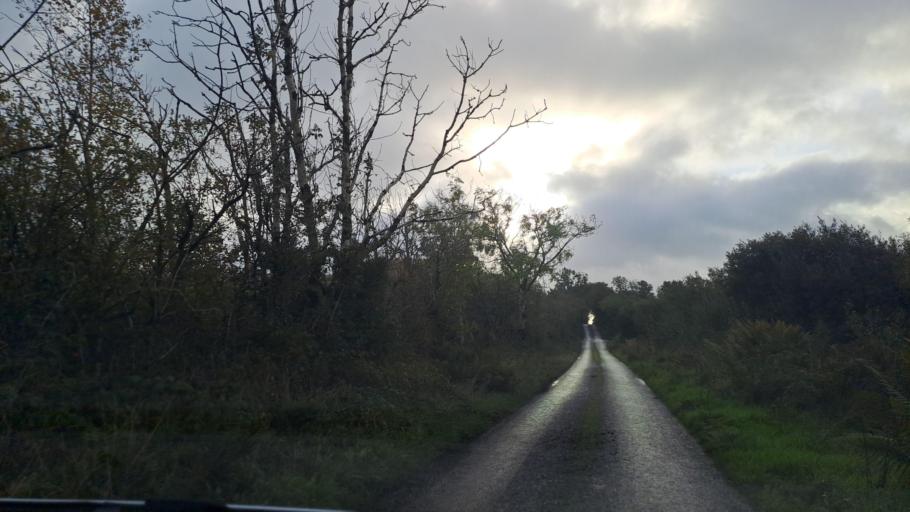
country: IE
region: Ulster
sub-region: An Cabhan
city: Kingscourt
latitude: 53.9633
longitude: -6.8254
